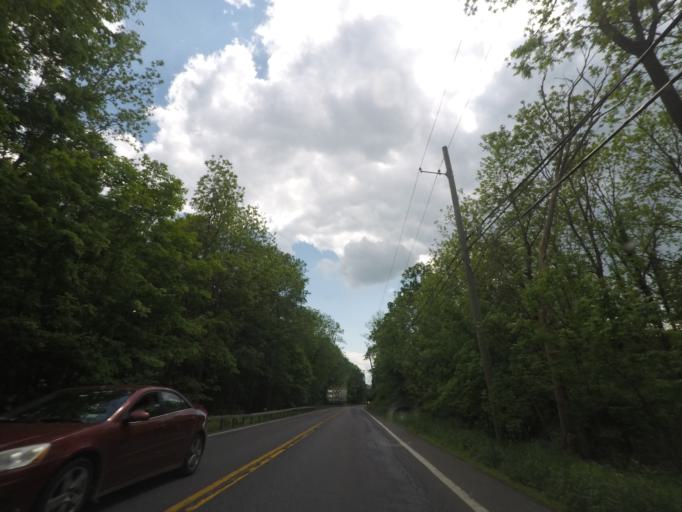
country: US
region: New York
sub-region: Dutchess County
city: Dover Plains
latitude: 41.8784
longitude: -73.5323
